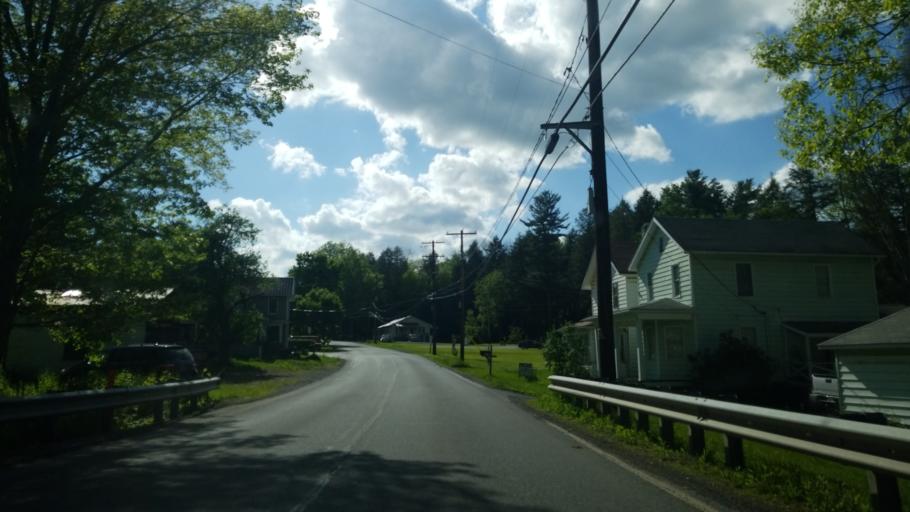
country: US
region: Pennsylvania
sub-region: Clearfield County
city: Troy
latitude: 40.9285
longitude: -78.2824
